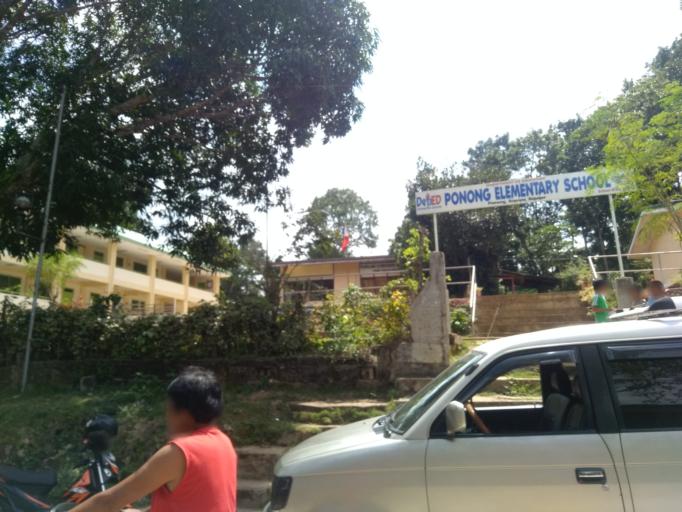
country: PH
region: Central Visayas
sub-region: Province of Siquijor
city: San Juan
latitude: 9.1586
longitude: 123.5540
